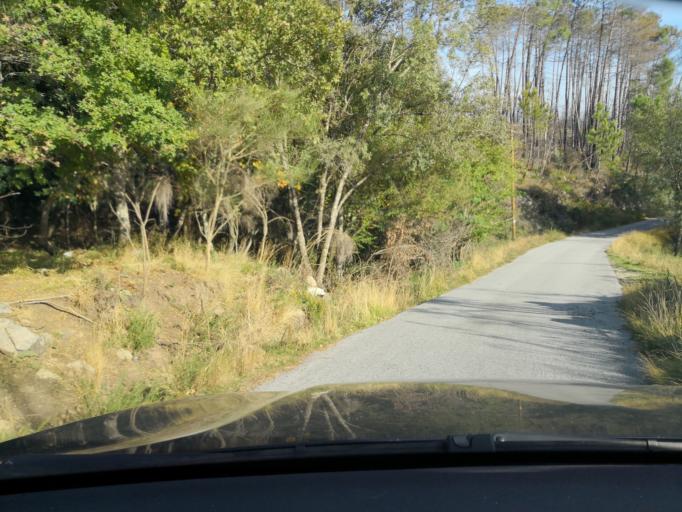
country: PT
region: Vila Real
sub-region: Vila Real
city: Vila Real
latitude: 41.3417
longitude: -7.7519
